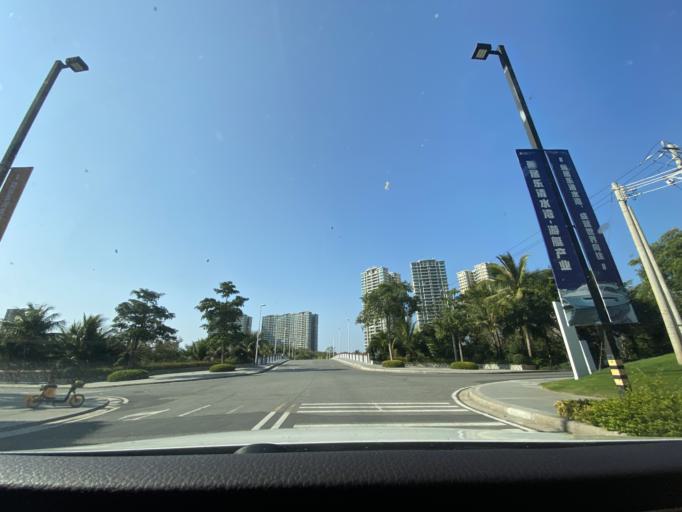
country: CN
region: Hainan
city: Yingzhou
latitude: 18.4093
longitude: 109.8807
